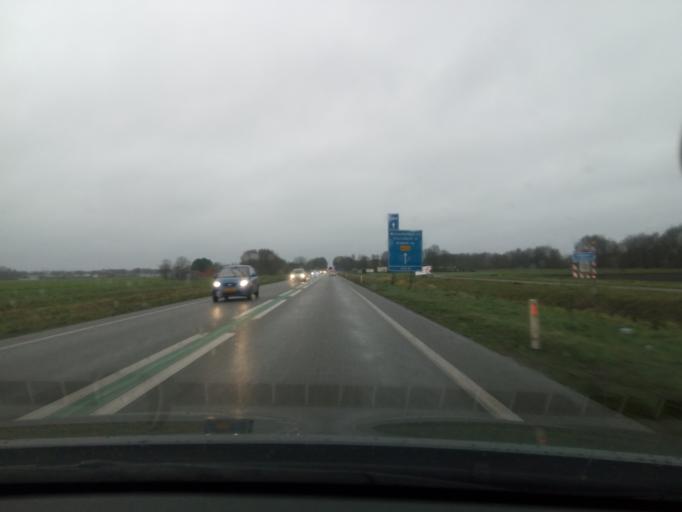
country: NL
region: Groningen
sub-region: Gemeente Appingedam
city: Appingedam
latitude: 53.2561
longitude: 6.8756
